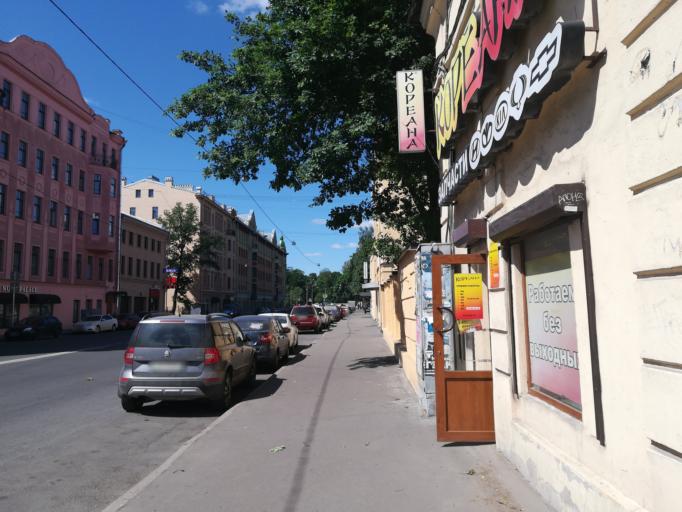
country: RU
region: St.-Petersburg
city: Vasyl'evsky Ostrov
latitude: 59.9454
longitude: 30.2590
